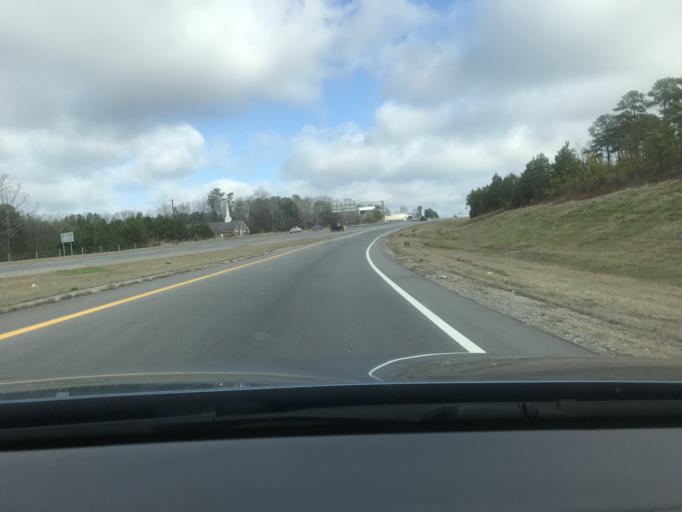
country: US
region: North Carolina
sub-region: Lee County
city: Sanford
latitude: 35.5142
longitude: -79.1865
